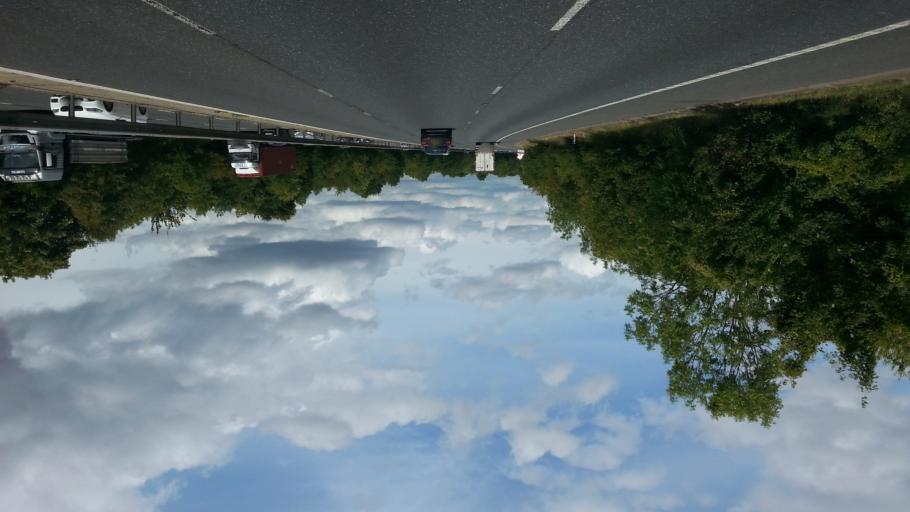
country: GB
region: England
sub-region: Essex
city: Little Hallingbury
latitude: 51.8299
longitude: 0.1909
